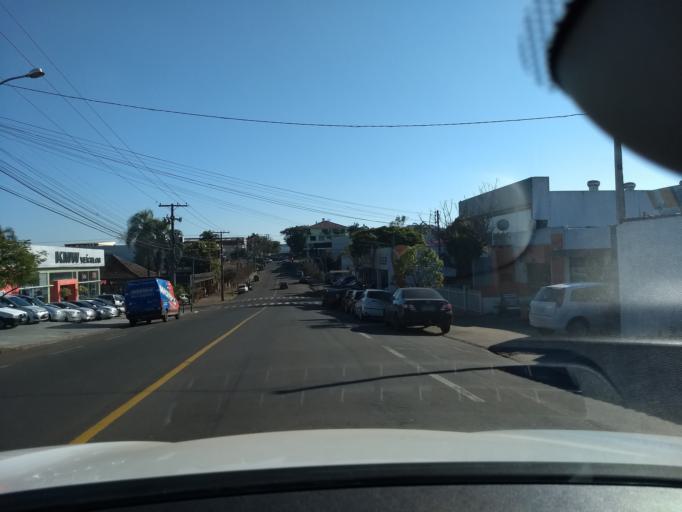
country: BR
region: Rio Grande do Sul
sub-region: Santa Cruz Do Sul
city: Santa Cruz do Sul
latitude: -29.7178
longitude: -52.4415
